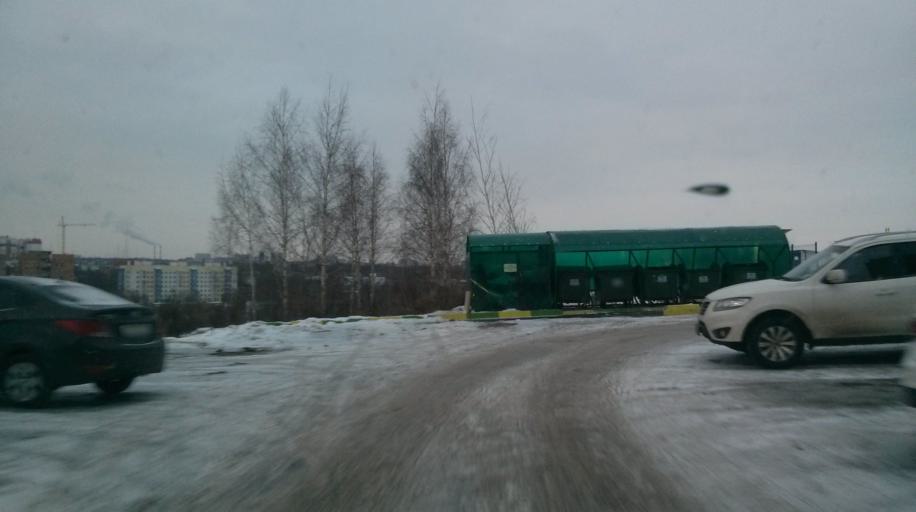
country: RU
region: Nizjnij Novgorod
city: Afonino
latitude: 56.2835
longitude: 44.0607
